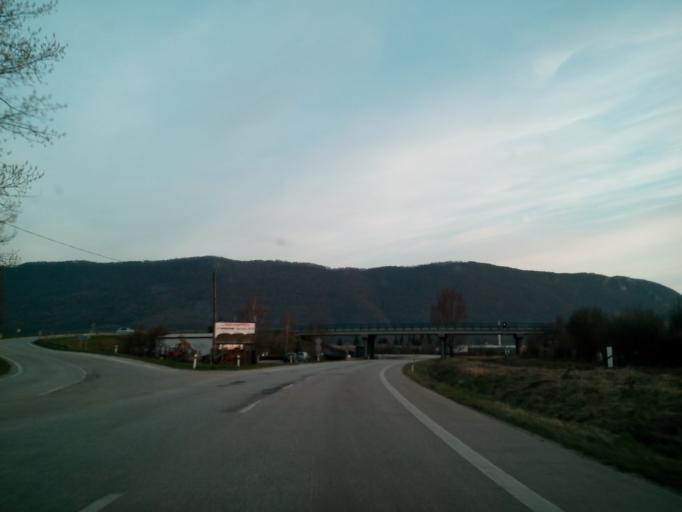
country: SK
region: Kosicky
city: Roznava
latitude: 48.6436
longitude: 20.5254
